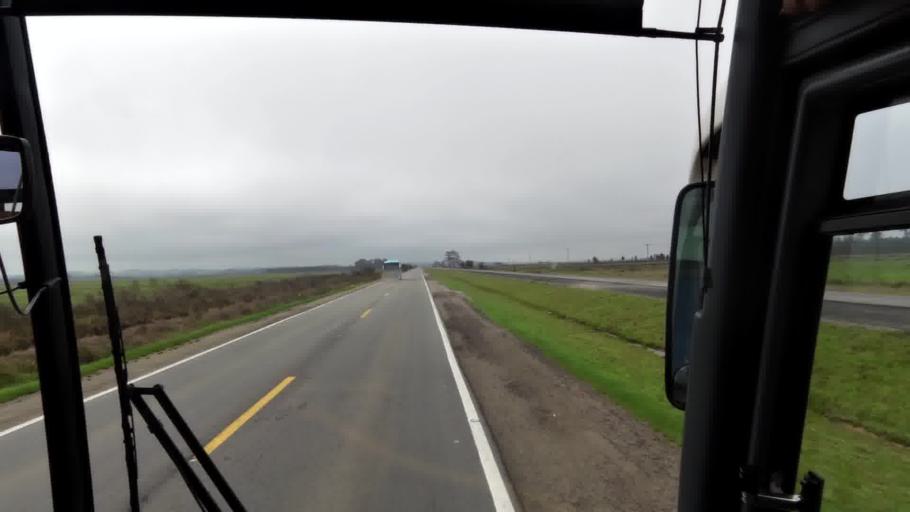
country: BR
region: Rio Grande do Sul
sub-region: Pelotas
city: Pelotas
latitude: -31.5940
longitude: -52.2855
